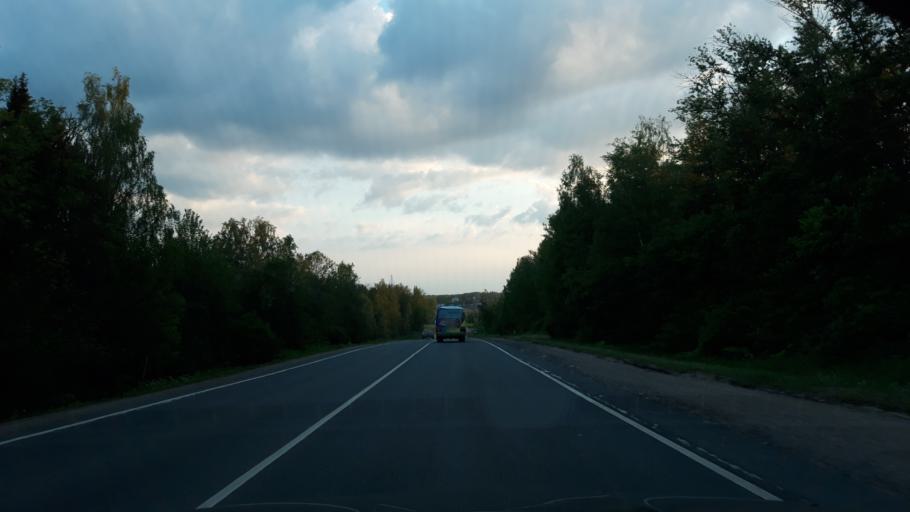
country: RU
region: Moskovskaya
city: Radumlya
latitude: 56.1124
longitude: 37.2032
